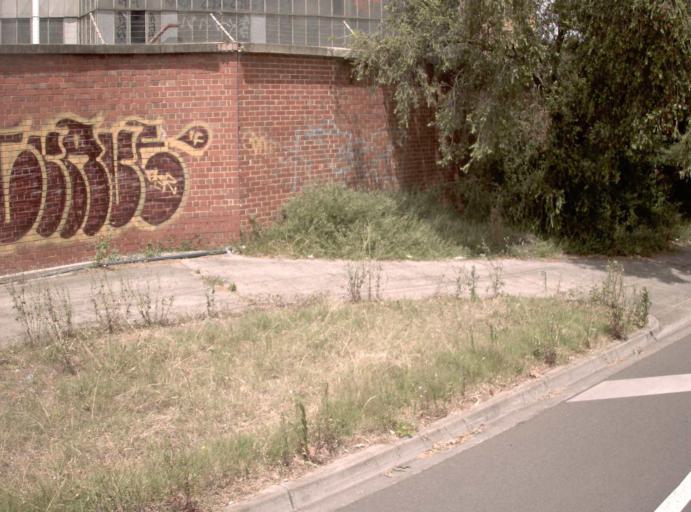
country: AU
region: Victoria
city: Alphington
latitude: -37.7852
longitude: 145.0253
